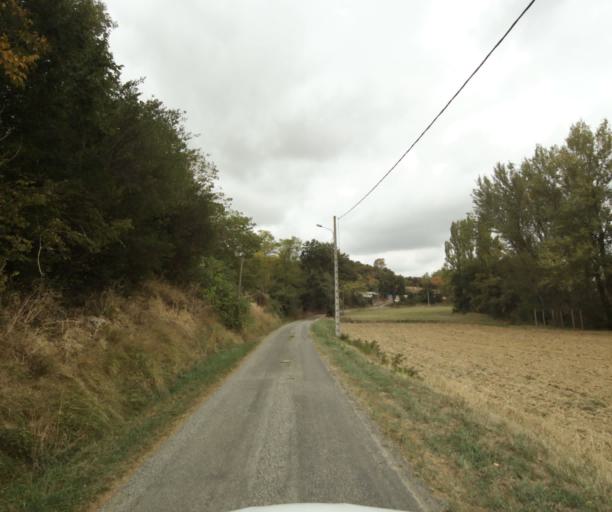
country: FR
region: Midi-Pyrenees
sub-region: Departement de la Haute-Garonne
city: Villefranche-de-Lauragais
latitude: 43.4098
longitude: 1.7172
